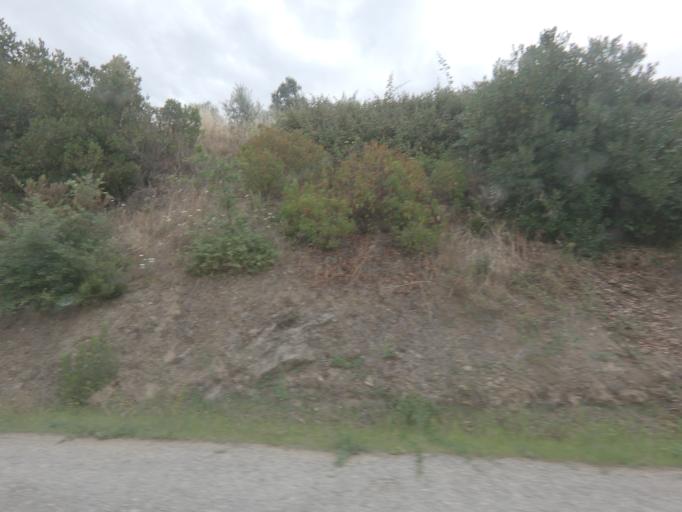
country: PT
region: Viseu
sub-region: Armamar
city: Armamar
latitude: 41.1257
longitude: -7.6468
